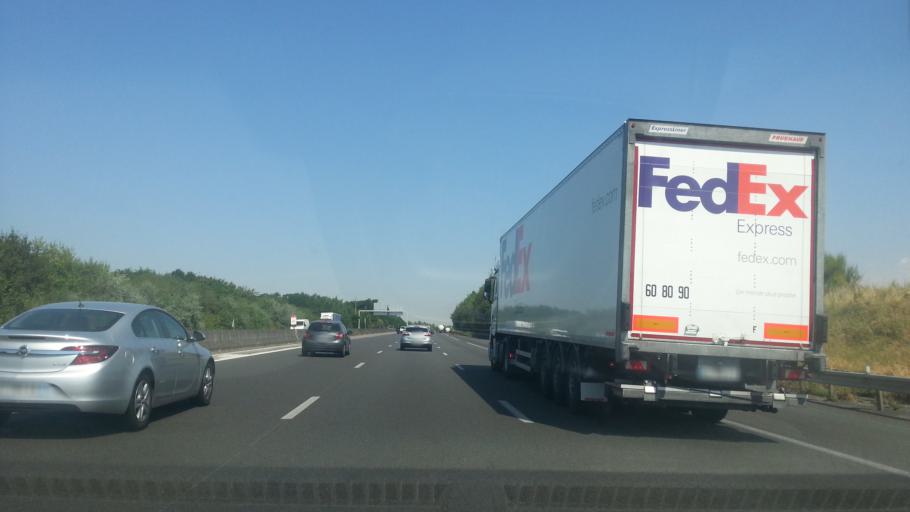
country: FR
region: Centre
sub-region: Departement du Loiret
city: Saint-Jean-de-la-Ruelle
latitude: 47.9169
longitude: 1.8489
